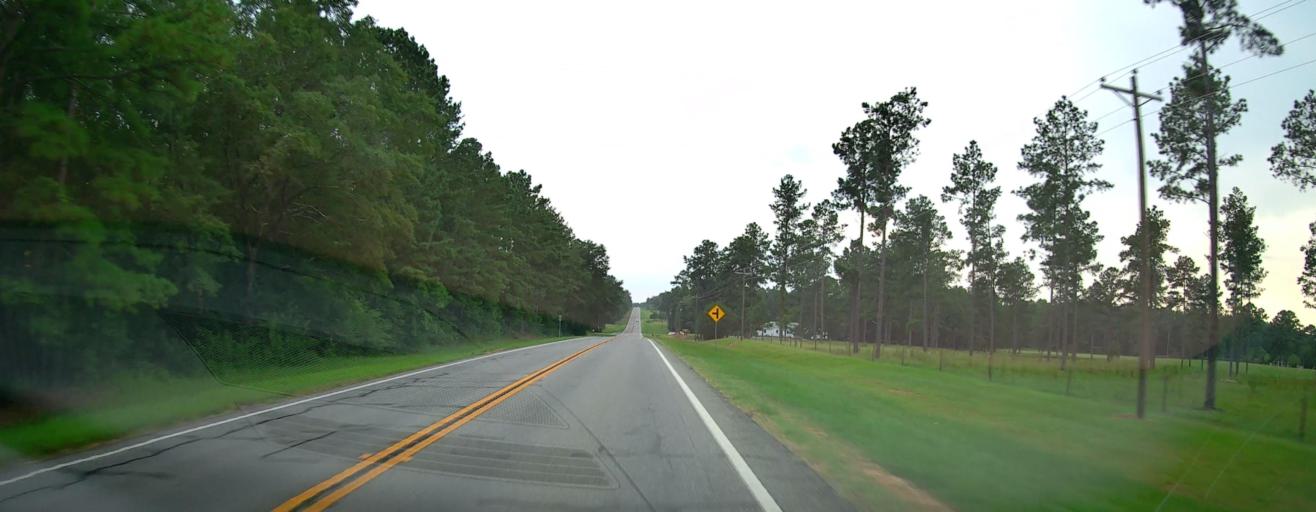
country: US
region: Georgia
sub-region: Laurens County
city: East Dublin
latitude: 32.6326
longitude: -82.8073
